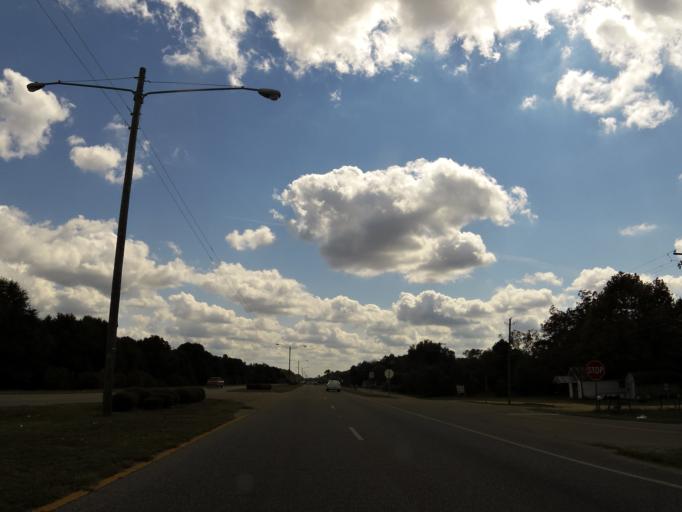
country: US
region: Alabama
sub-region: Dallas County
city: Selma
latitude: 32.3946
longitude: -87.0145
